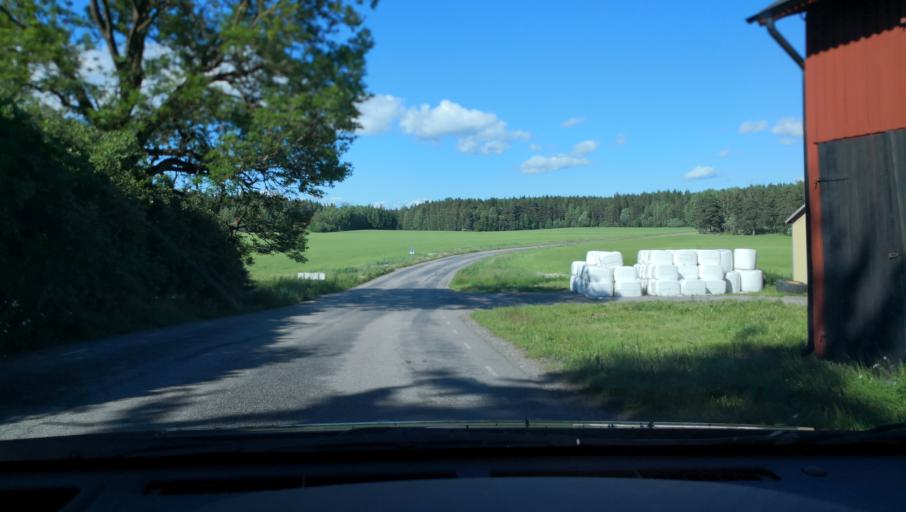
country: SE
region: Soedermanland
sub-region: Eskilstuna Kommun
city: Arla
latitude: 59.3216
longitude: 16.6096
